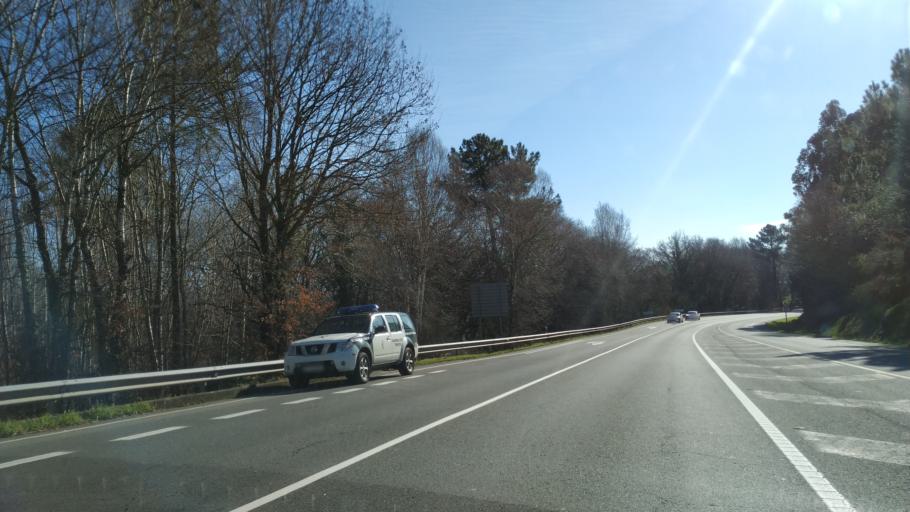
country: ES
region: Galicia
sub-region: Provincia de Pontevedra
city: Silleda
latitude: 42.6909
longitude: -8.2226
